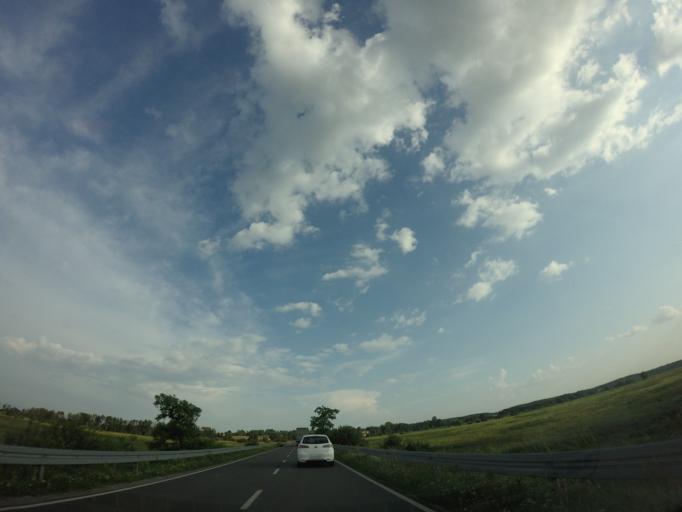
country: PL
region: Lublin Voivodeship
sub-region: Powiat lubartowski
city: Jeziorzany
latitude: 51.5956
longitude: 22.2803
